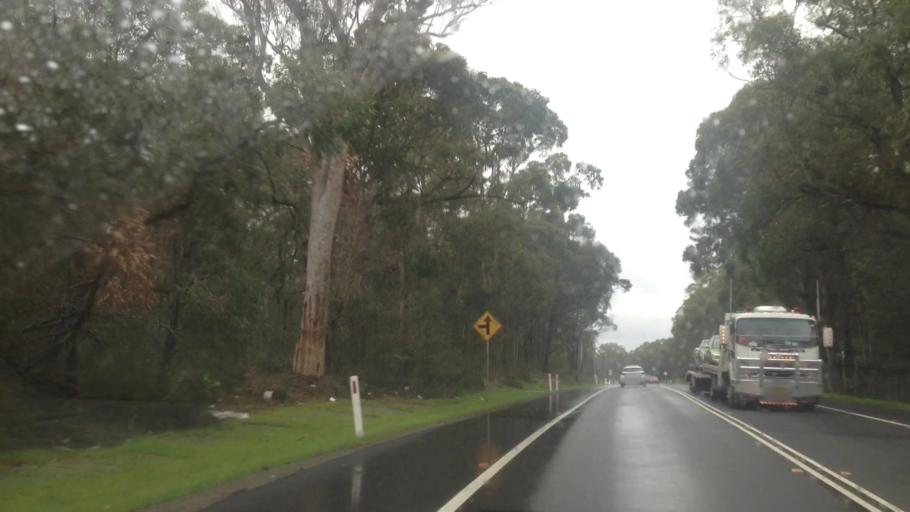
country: AU
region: New South Wales
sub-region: Lake Macquarie Shire
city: Dora Creek
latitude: -33.1232
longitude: 151.4758
